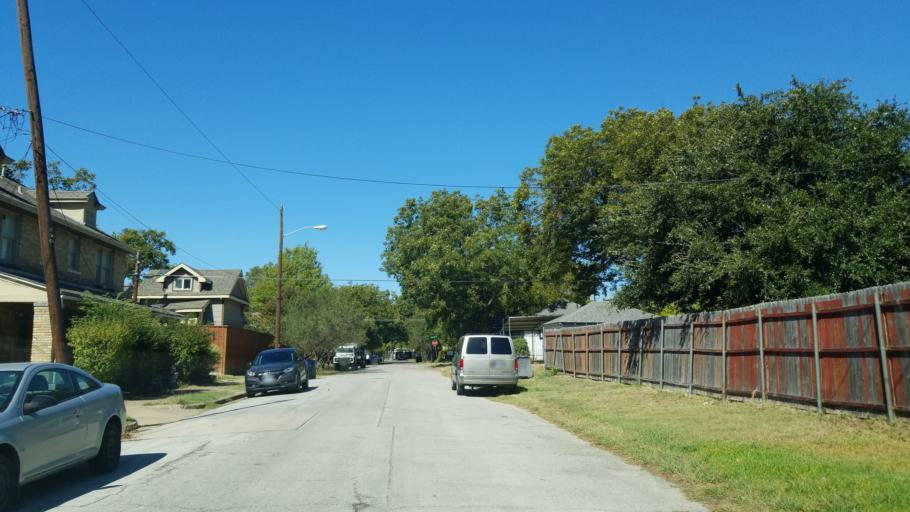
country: US
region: Texas
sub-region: Dallas County
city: Highland Park
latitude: 32.8047
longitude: -96.7578
